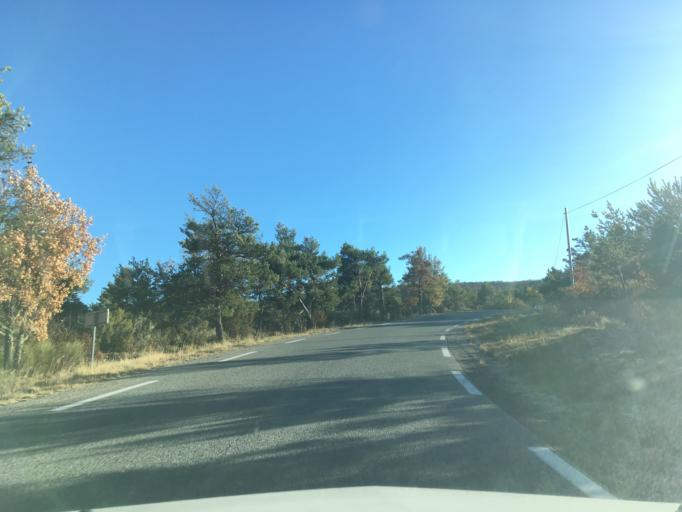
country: FR
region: Provence-Alpes-Cote d'Azur
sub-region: Departement des Alpes-de-Haute-Provence
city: Castellane
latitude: 43.7419
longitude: 6.4367
